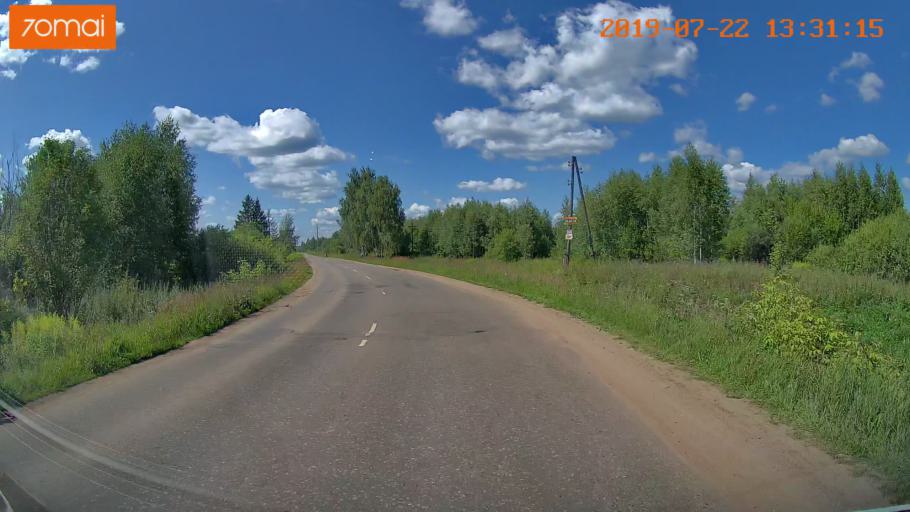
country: RU
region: Ivanovo
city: Novo-Talitsy
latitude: 57.0571
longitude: 40.9185
